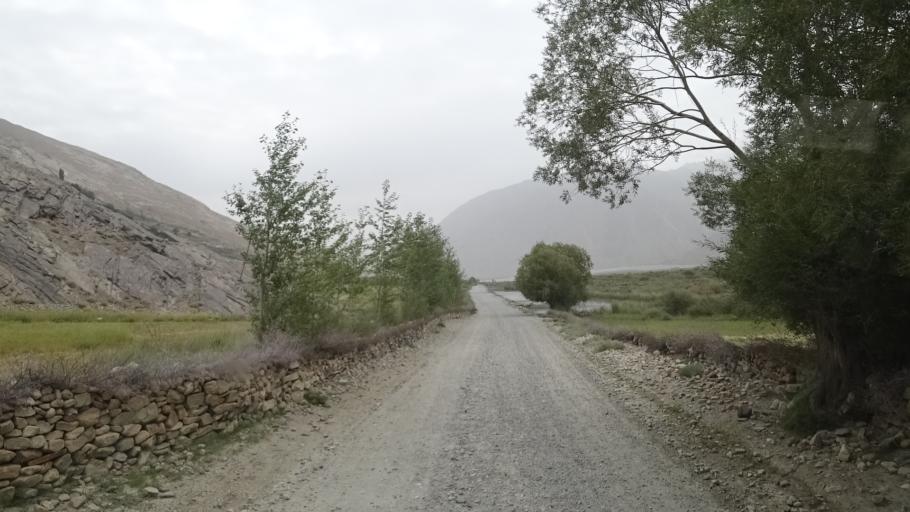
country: AF
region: Badakhshan
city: Khandud
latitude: 37.0047
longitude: 72.5209
